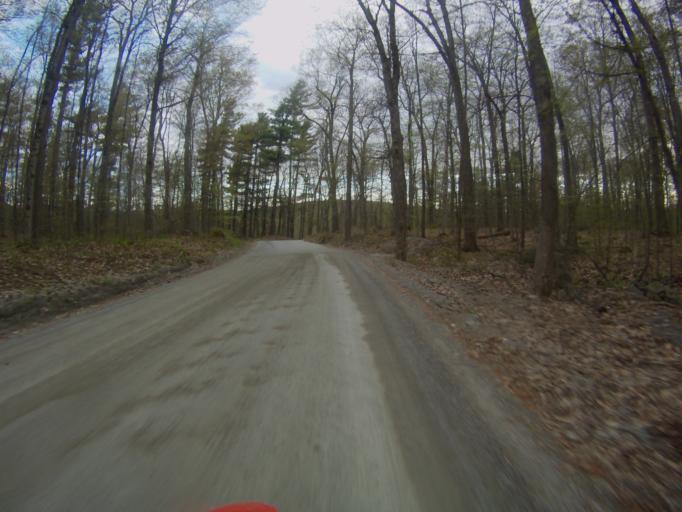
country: US
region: Vermont
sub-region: Addison County
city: Middlebury (village)
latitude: 43.9724
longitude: -73.0847
